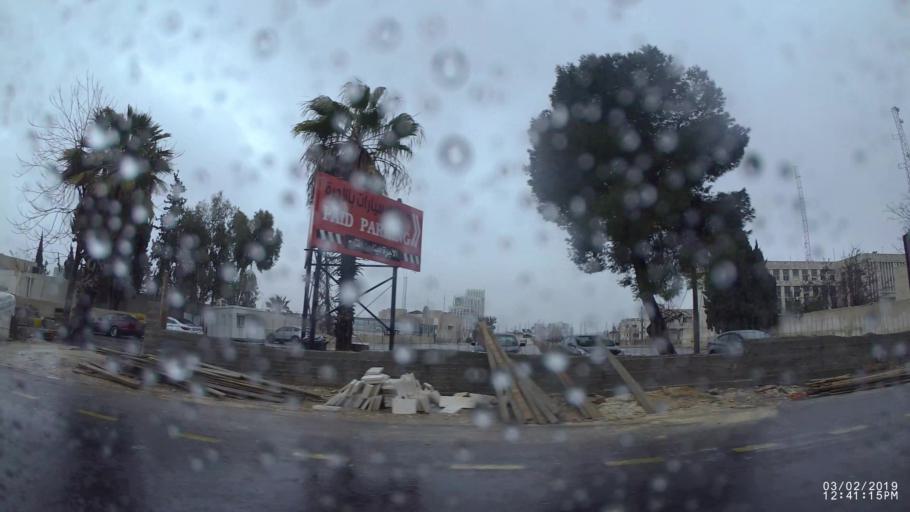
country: JO
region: Amman
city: Amman
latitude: 31.9608
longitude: 35.9105
